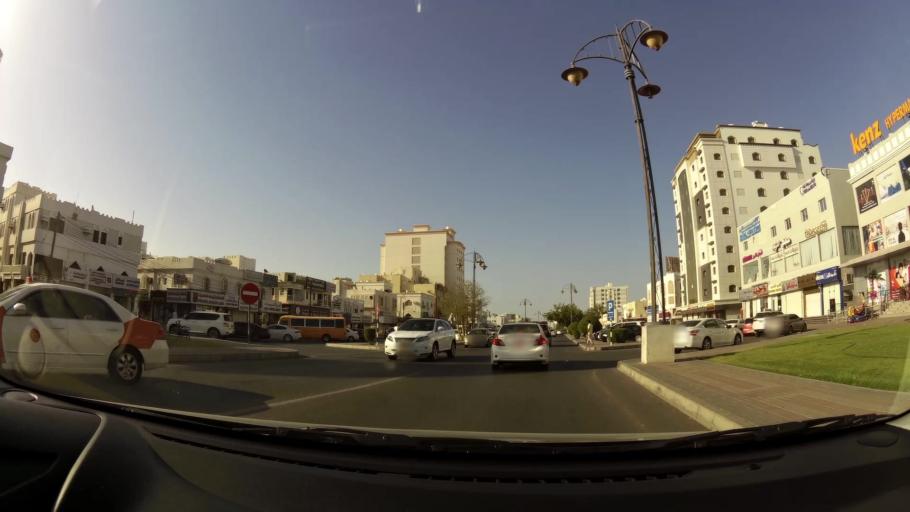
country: OM
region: Muhafazat Masqat
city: As Sib al Jadidah
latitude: 23.6298
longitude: 58.1973
